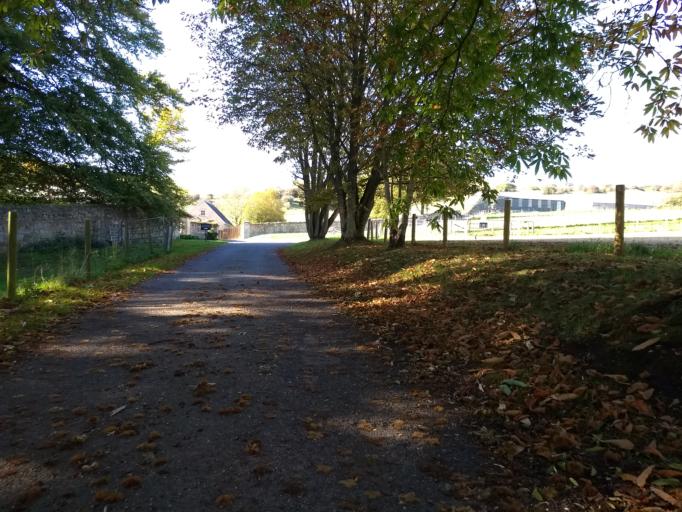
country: GB
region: England
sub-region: Isle of Wight
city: Ventnor
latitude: 50.6183
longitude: -1.2334
